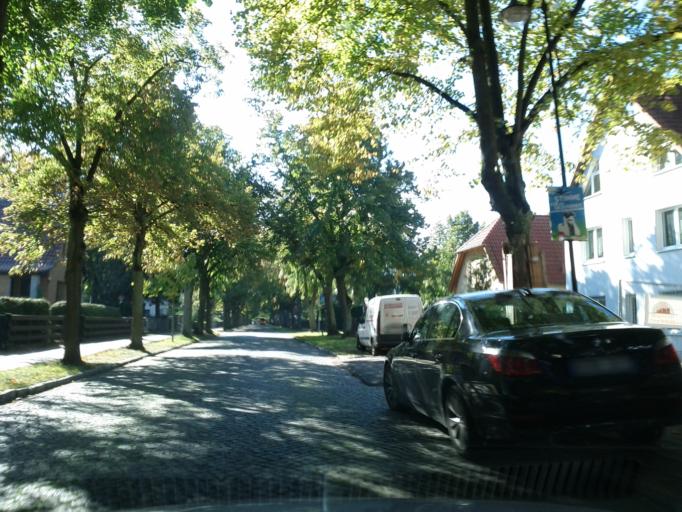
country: DE
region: Brandenburg
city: Schoneiche
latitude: 52.4637
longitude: 13.6989
